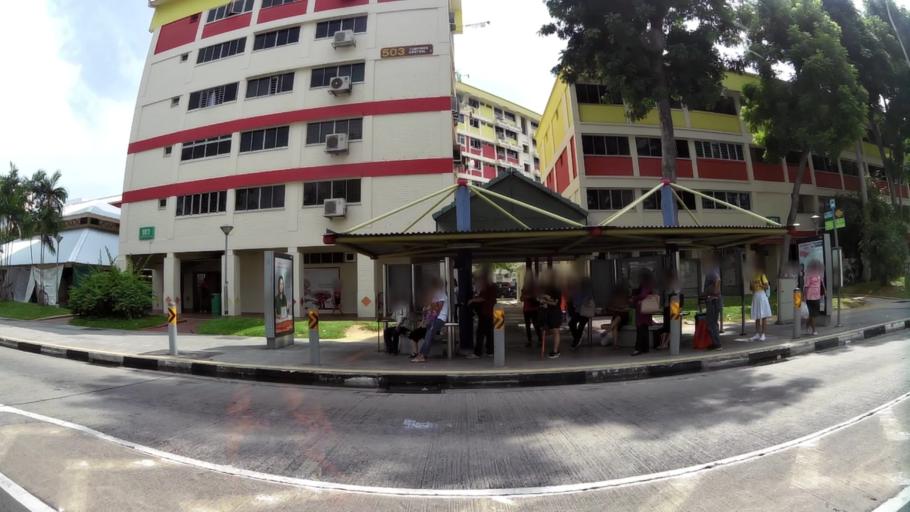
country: SG
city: Singapore
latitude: 1.3567
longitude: 103.9453
